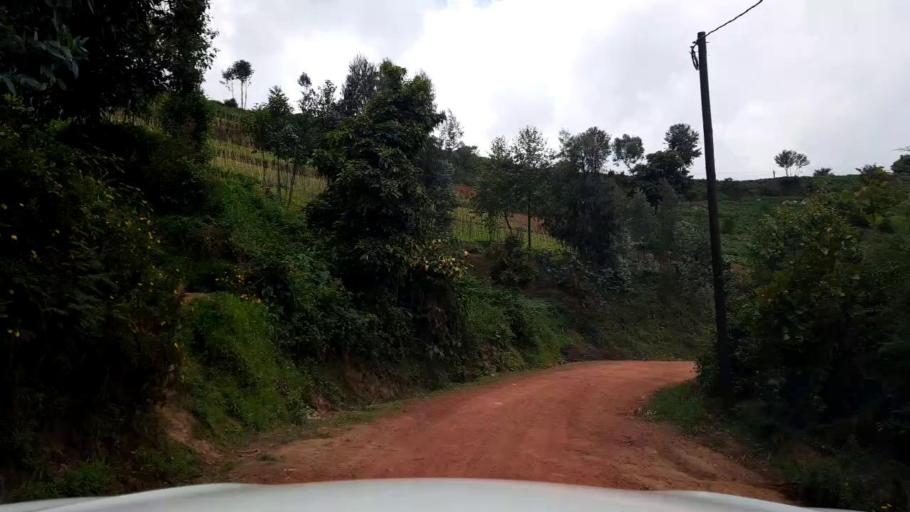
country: RW
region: Northern Province
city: Byumba
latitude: -1.4866
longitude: 29.9290
